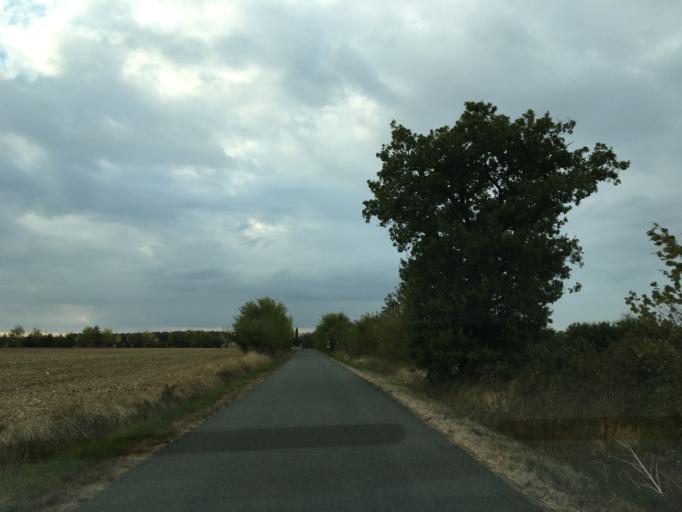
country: FR
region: Poitou-Charentes
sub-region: Departement des Deux-Sevres
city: Beauvoir-sur-Niort
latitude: 46.0869
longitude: -0.5016
